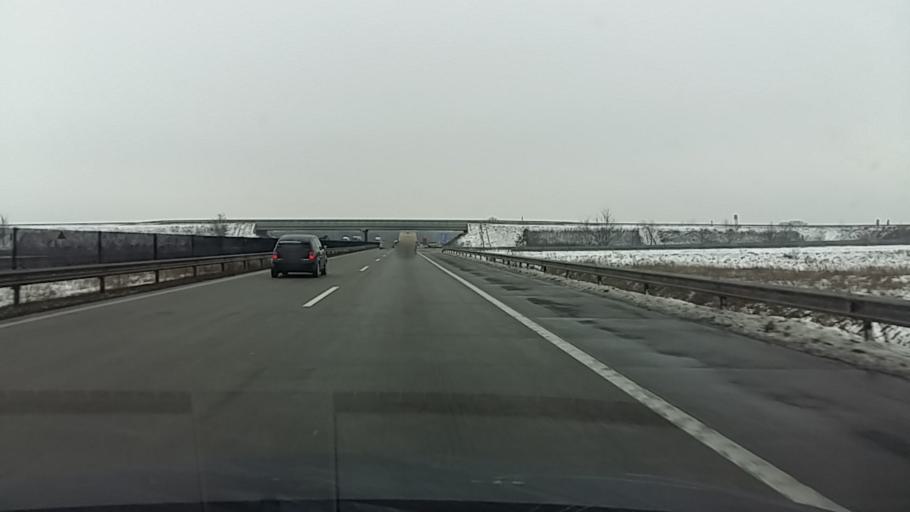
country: HU
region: Pest
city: Ecser
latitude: 47.4327
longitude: 19.3274
